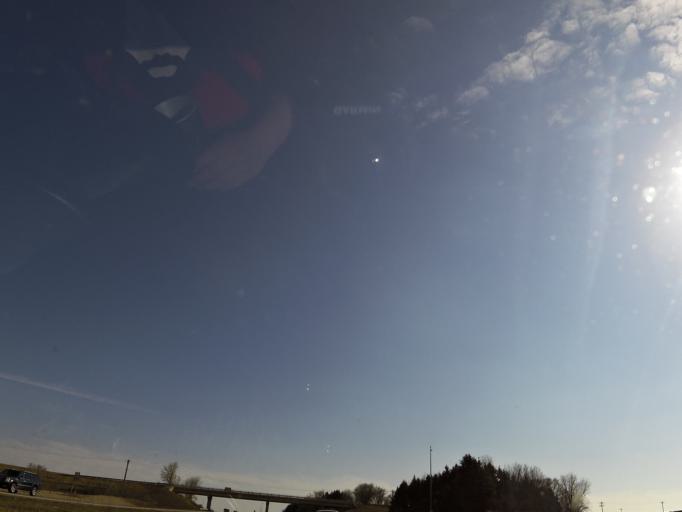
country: US
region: Minnesota
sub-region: Steele County
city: Owatonna
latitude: 44.0722
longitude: -93.2524
